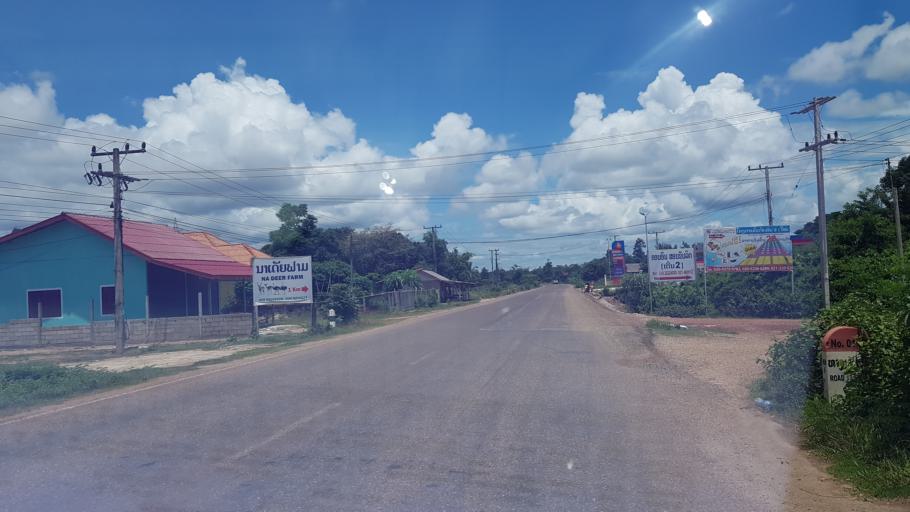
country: LA
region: Vientiane
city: Vientiane
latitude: 18.1071
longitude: 102.5742
